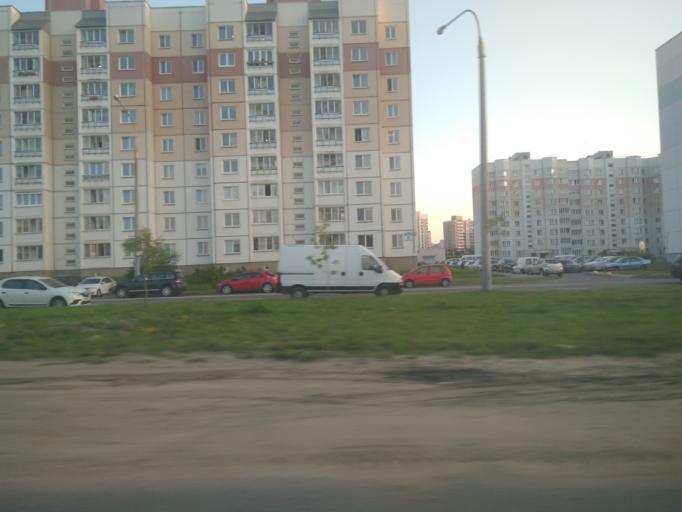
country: BY
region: Minsk
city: Novoye Medvezhino
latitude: 53.9219
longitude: 27.4600
